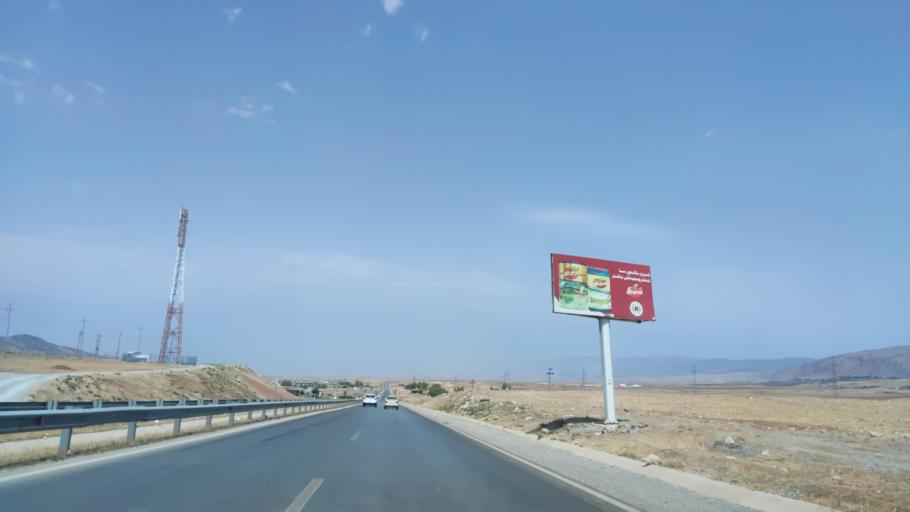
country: IQ
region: Arbil
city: Shaqlawah
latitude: 36.4946
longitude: 44.3675
